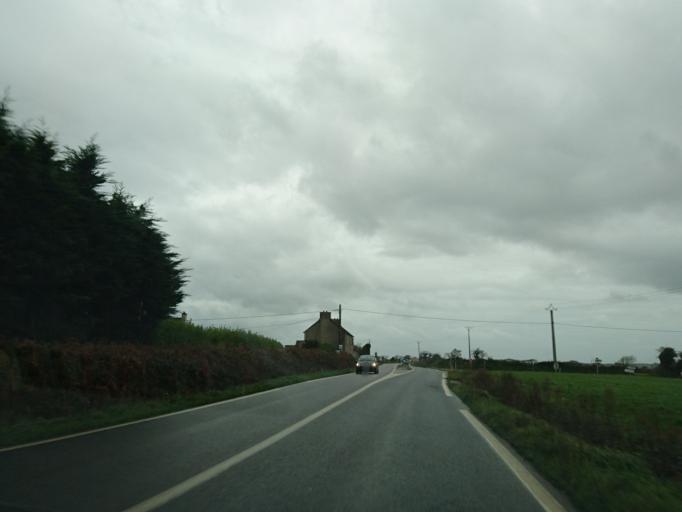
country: FR
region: Brittany
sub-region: Departement du Finistere
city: Plouzane
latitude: 48.3617
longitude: -4.6147
